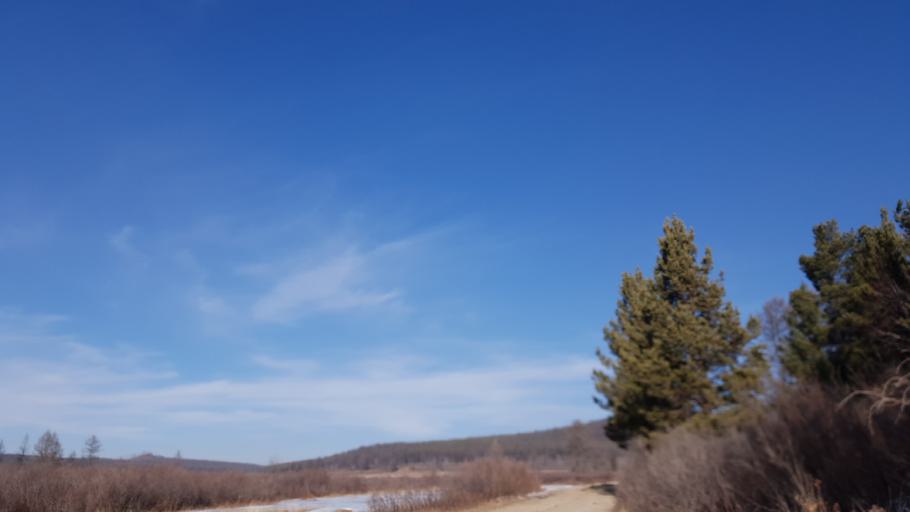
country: MN
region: Ulaanbaatar
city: Ulaanbaatar
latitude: 48.1594
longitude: 106.8824
